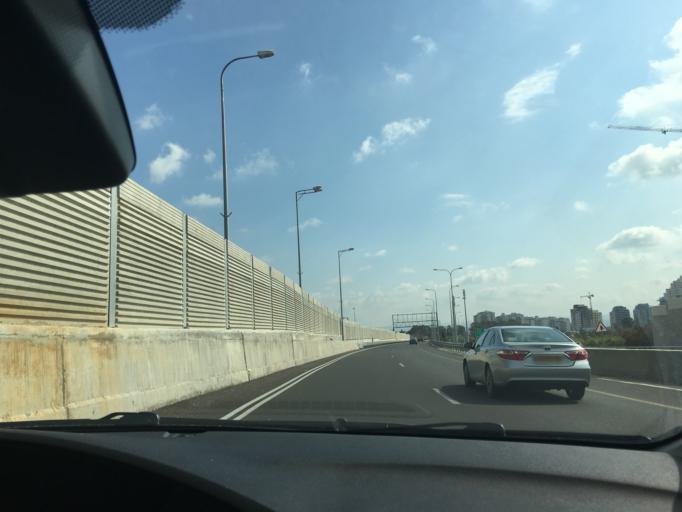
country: IL
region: Central District
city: Kfar Saba
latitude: 32.1713
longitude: 34.8959
